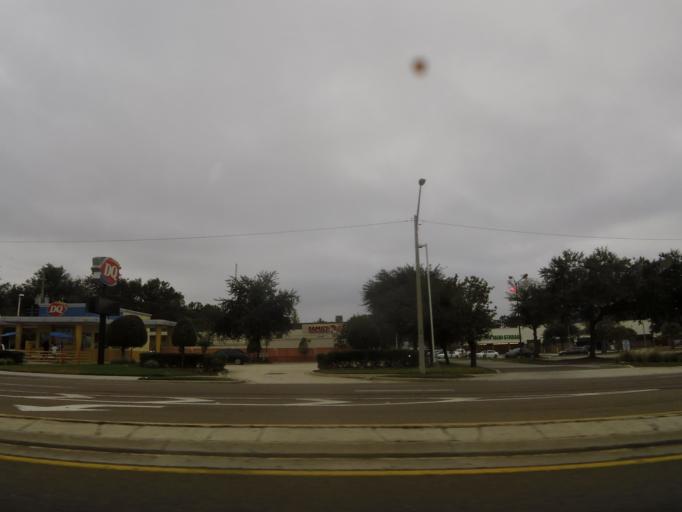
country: US
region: Florida
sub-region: Clay County
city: Bellair-Meadowbrook Terrace
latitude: 30.2480
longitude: -81.7657
